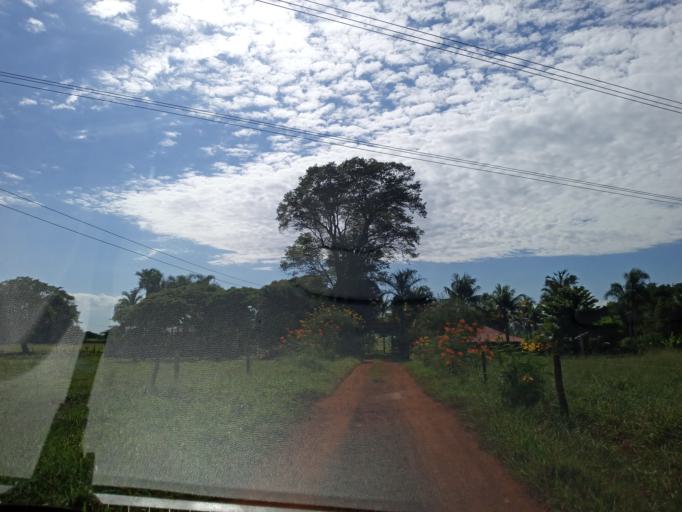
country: BR
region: Goias
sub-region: Itumbiara
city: Itumbiara
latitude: -18.4606
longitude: -49.1130
